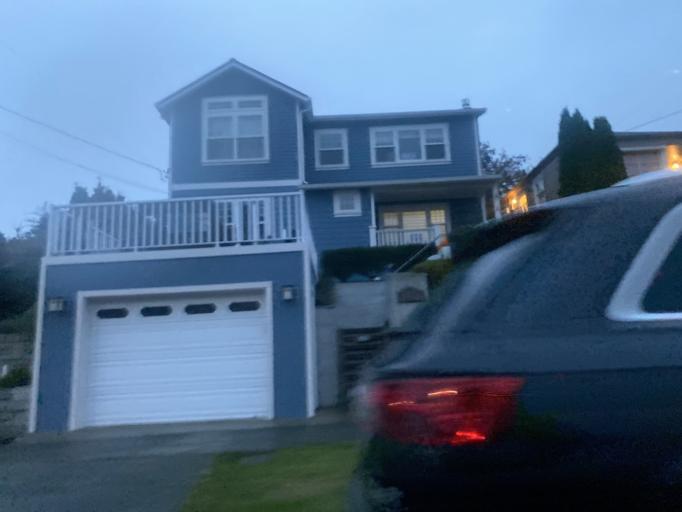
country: US
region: Washington
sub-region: King County
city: Seattle
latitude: 47.6409
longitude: -122.3942
